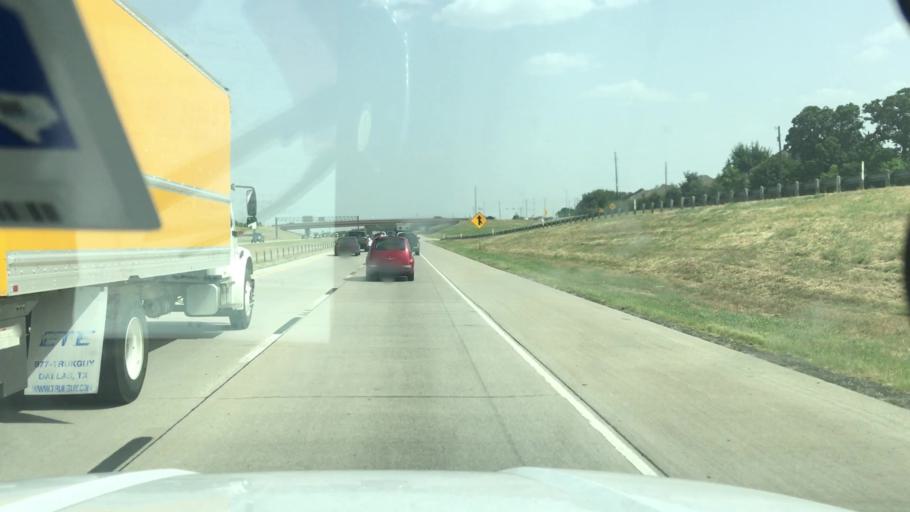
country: US
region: Texas
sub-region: Tarrant County
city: Euless
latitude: 32.8850
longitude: -97.0781
